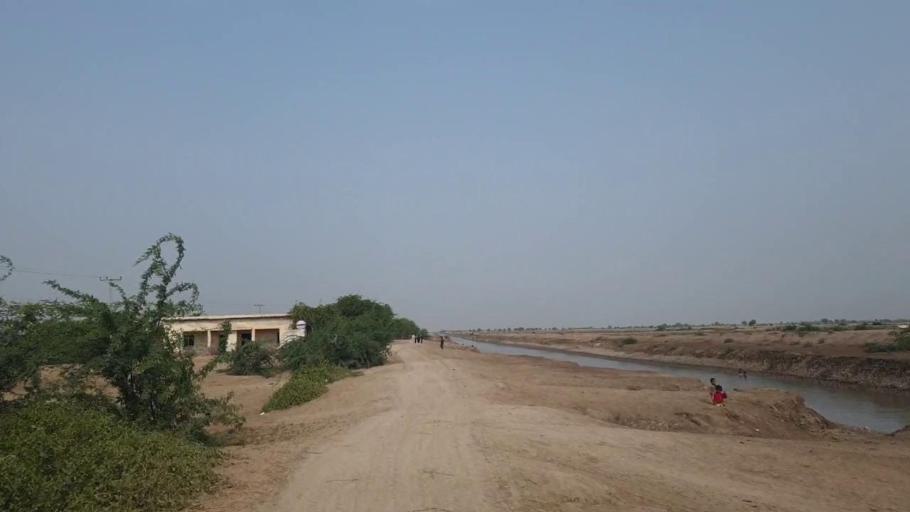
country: PK
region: Sindh
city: Badin
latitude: 24.7165
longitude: 68.7715
